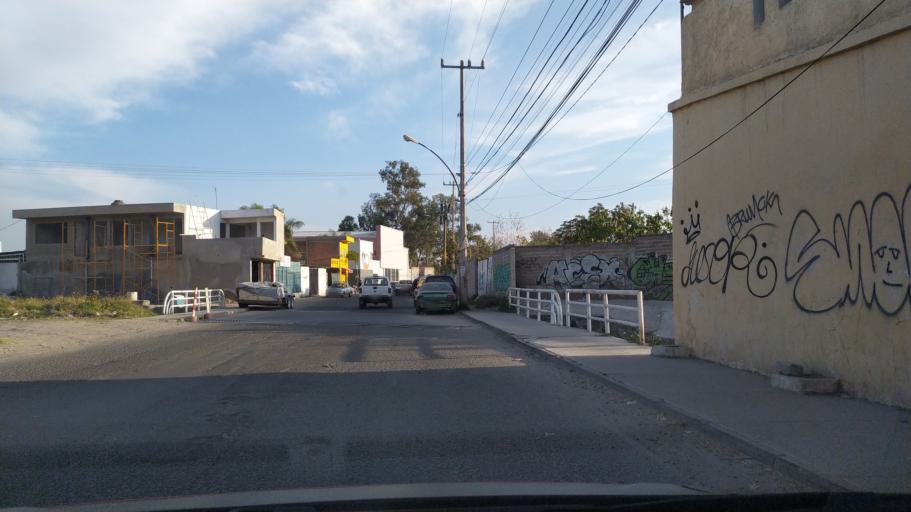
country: MX
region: Jalisco
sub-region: Tlajomulco de Zuniga
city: Palomar
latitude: 20.6280
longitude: -103.4554
